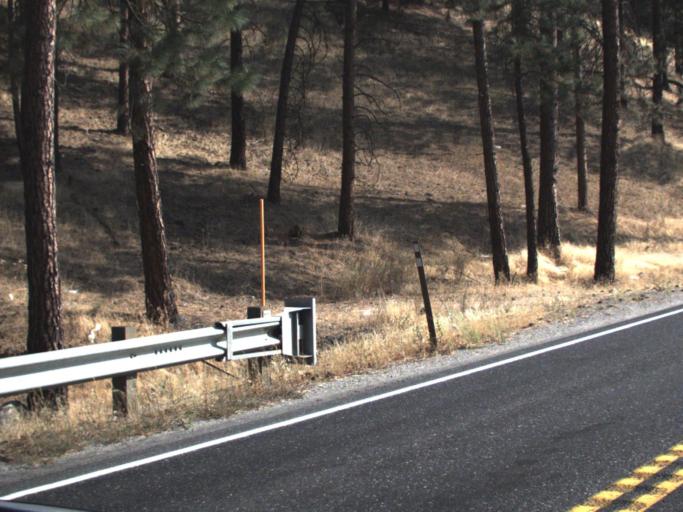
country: US
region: Washington
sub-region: Spokane County
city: Fairwood
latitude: 47.8037
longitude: -117.5500
